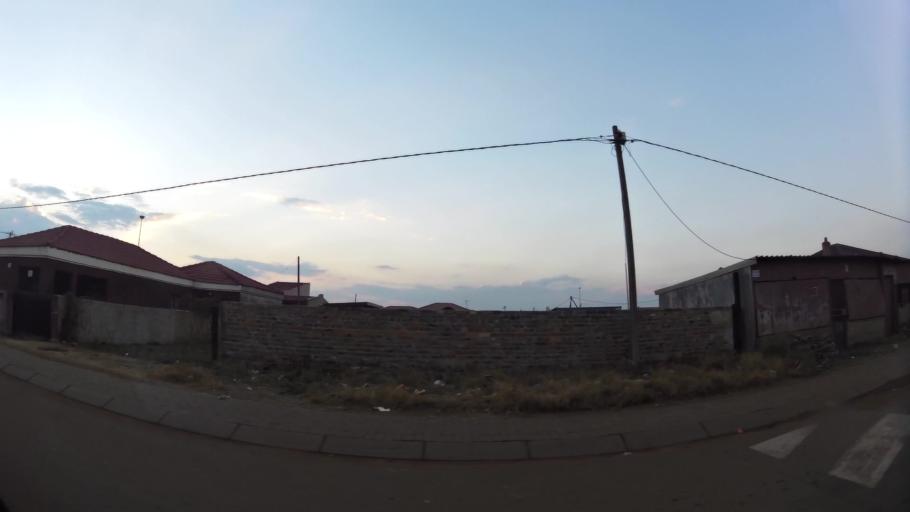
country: ZA
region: Gauteng
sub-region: City of Johannesburg Metropolitan Municipality
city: Orange Farm
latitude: -26.5562
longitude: 27.8747
